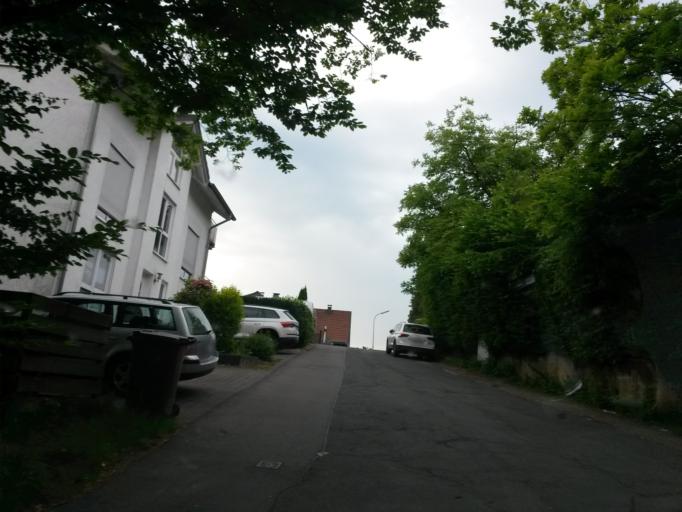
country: DE
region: North Rhine-Westphalia
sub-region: Regierungsbezirk Koln
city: Overath
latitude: 50.9293
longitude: 7.2742
